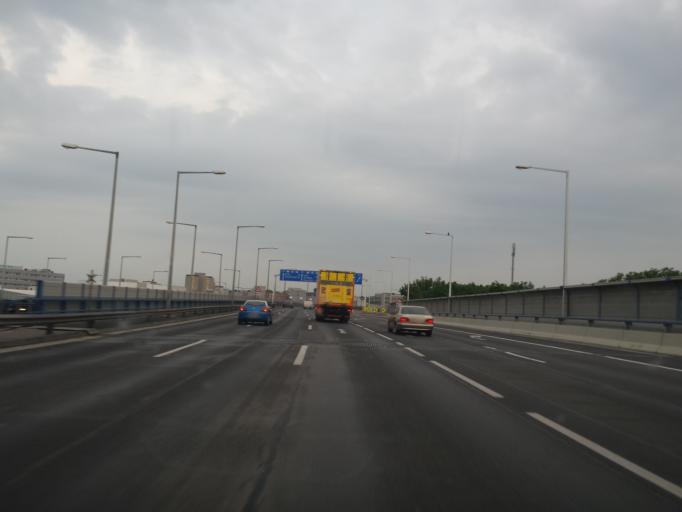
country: AT
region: Vienna
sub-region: Wien Stadt
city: Vienna
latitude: 48.1832
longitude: 16.4040
